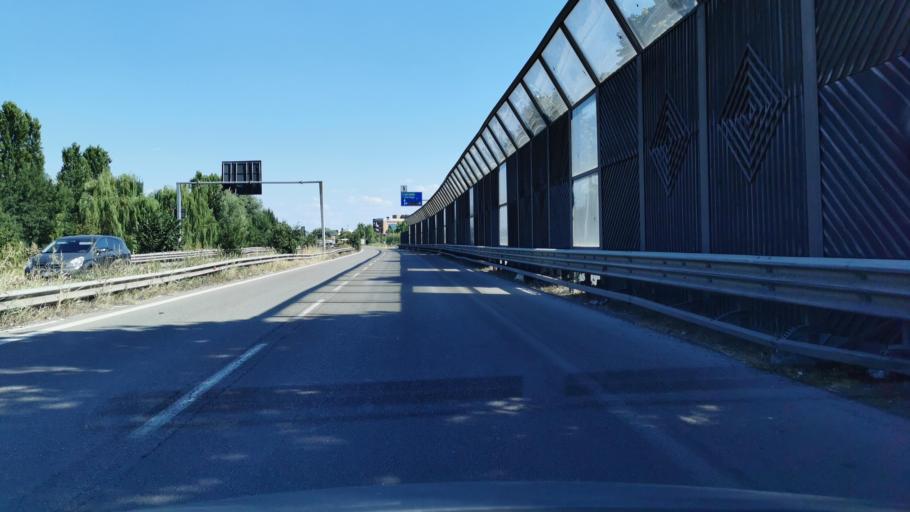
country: IT
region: Emilia-Romagna
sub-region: Provincia di Modena
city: Modena
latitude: 44.6561
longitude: 10.9550
